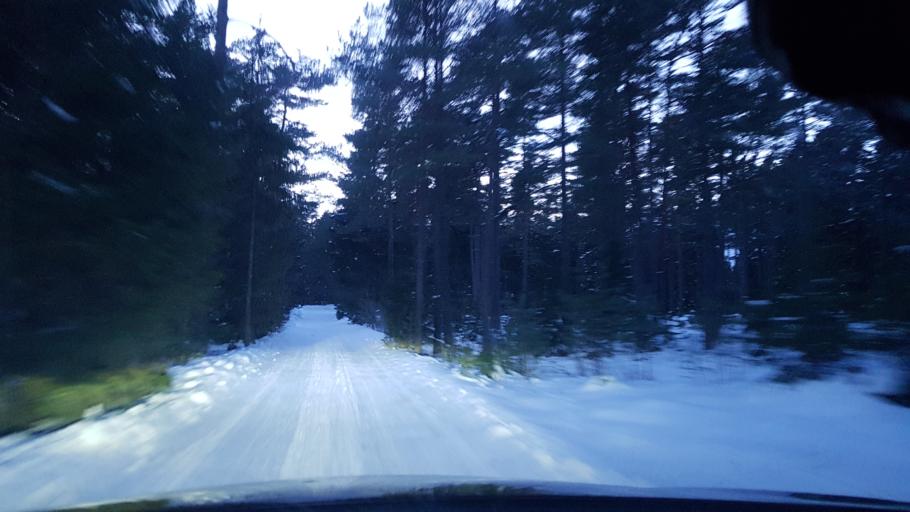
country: EE
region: Laeaene
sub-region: Haapsalu linn
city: Haapsalu
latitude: 59.2120
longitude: 23.5486
